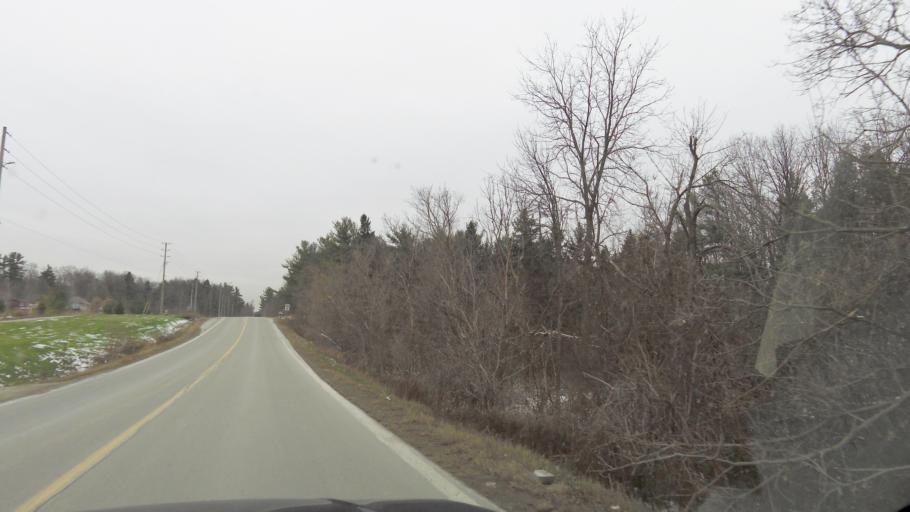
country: CA
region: Ontario
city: Vaughan
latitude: 43.8349
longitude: -79.5853
